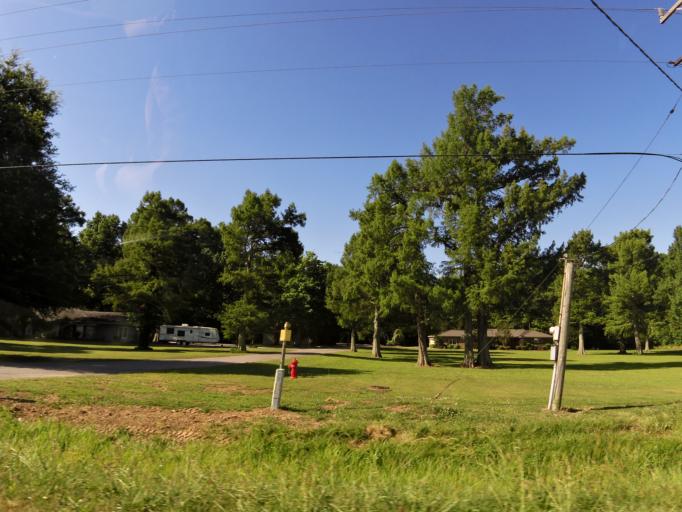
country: US
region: Arkansas
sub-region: Clay County
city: Corning
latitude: 36.4066
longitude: -90.5751
